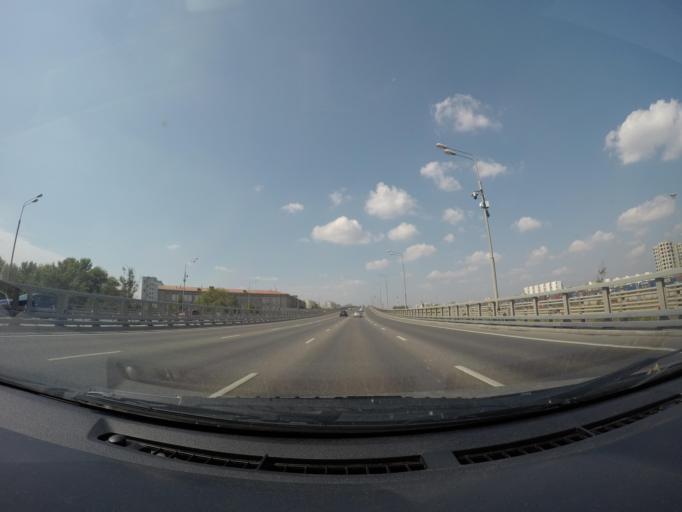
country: RU
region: Moscow
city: Zapadnoye Degunino
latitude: 55.8576
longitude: 37.5338
